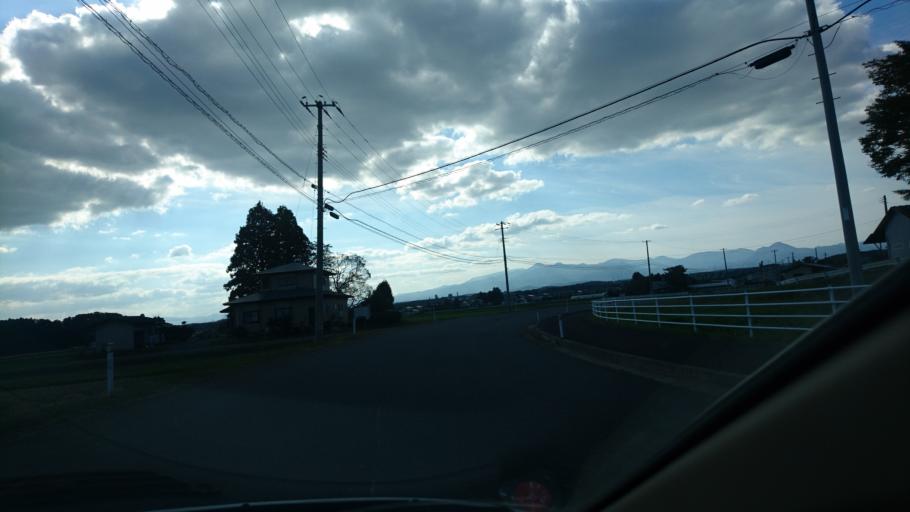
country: JP
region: Iwate
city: Kitakami
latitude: 39.2451
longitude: 141.1272
